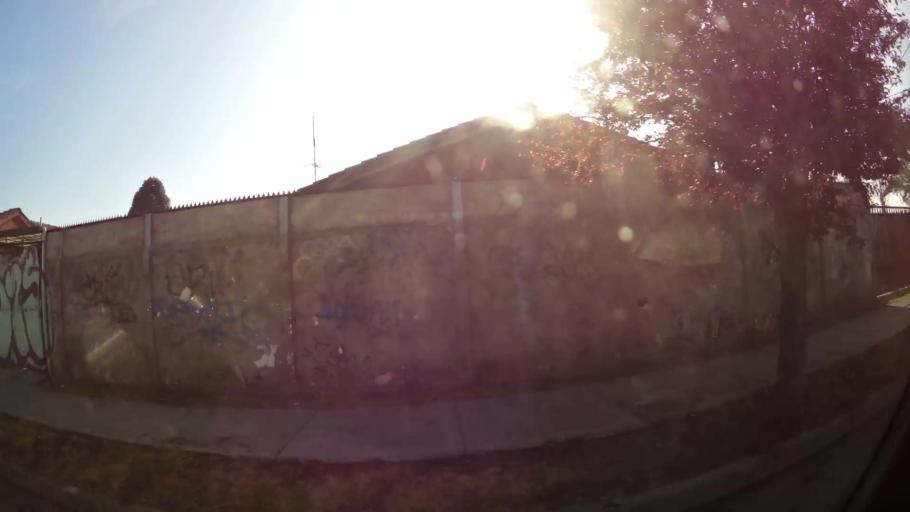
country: CL
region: Santiago Metropolitan
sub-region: Provincia de Santiago
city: Lo Prado
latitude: -33.4557
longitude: -70.7665
